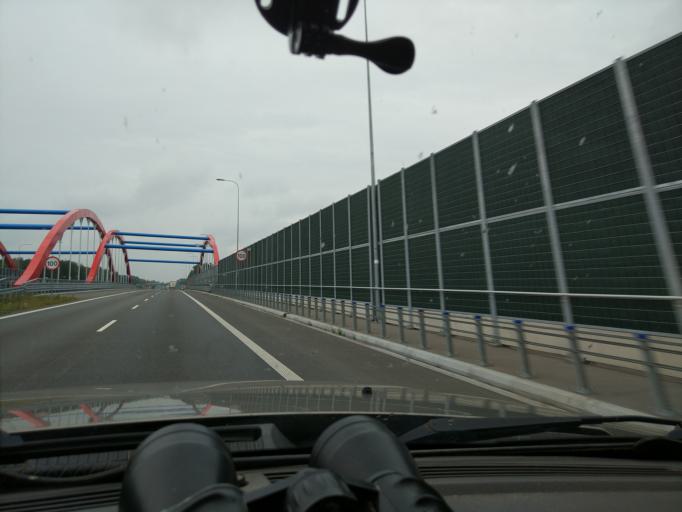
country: PL
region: Masovian Voivodeship
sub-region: Powiat ostrowski
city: Ostrow Mazowiecka
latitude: 52.8273
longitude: 21.9378
